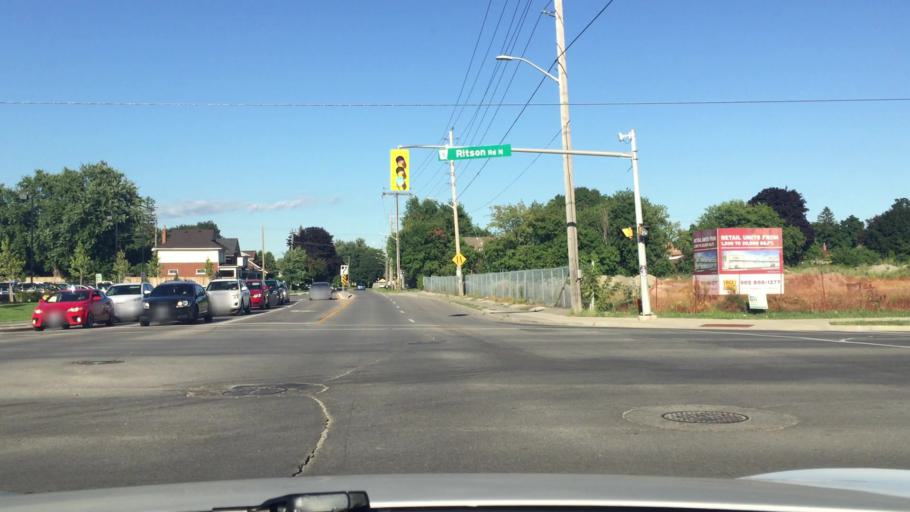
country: CA
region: Ontario
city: Oshawa
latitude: 43.9064
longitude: -78.8568
